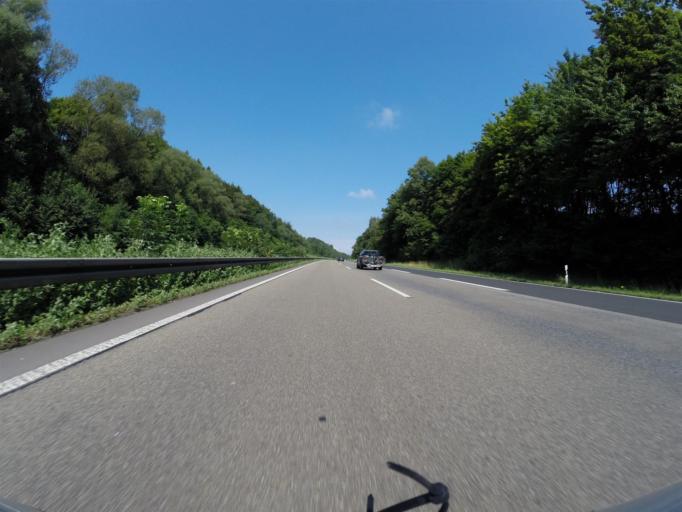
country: DE
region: Hesse
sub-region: Regierungsbezirk Kassel
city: Martinhagen
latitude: 51.3122
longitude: 9.2941
